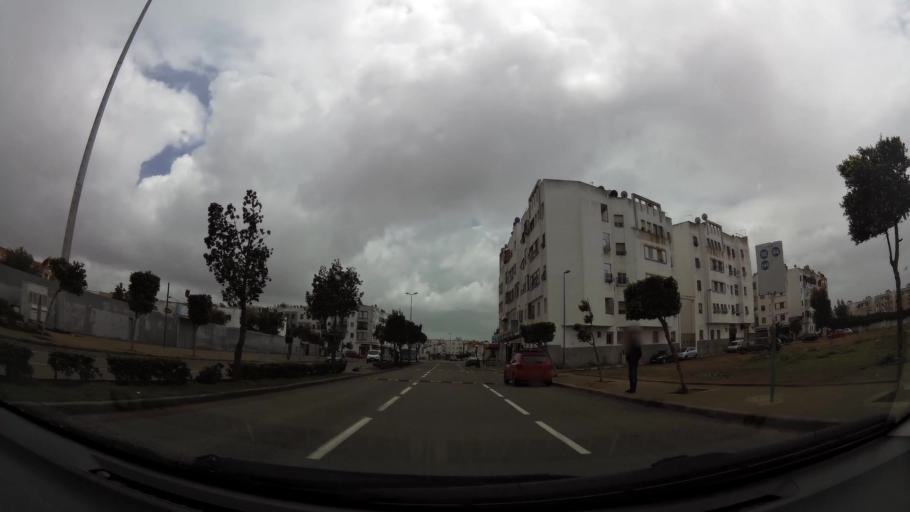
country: MA
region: Grand Casablanca
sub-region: Casablanca
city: Casablanca
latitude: 33.5458
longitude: -7.6864
